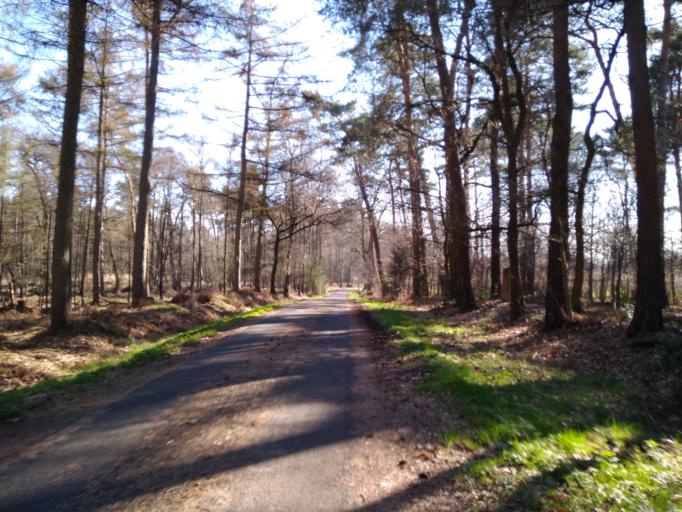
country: DE
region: North Rhine-Westphalia
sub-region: Regierungsbezirk Dusseldorf
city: Hunxe
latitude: 51.6401
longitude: 6.8303
